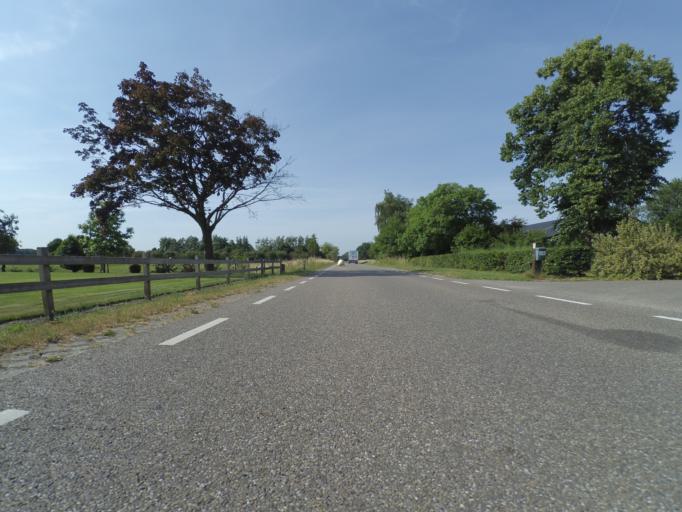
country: NL
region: North Brabant
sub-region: Gemeente Steenbergen
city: Welberg
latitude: 51.5281
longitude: 4.3299
